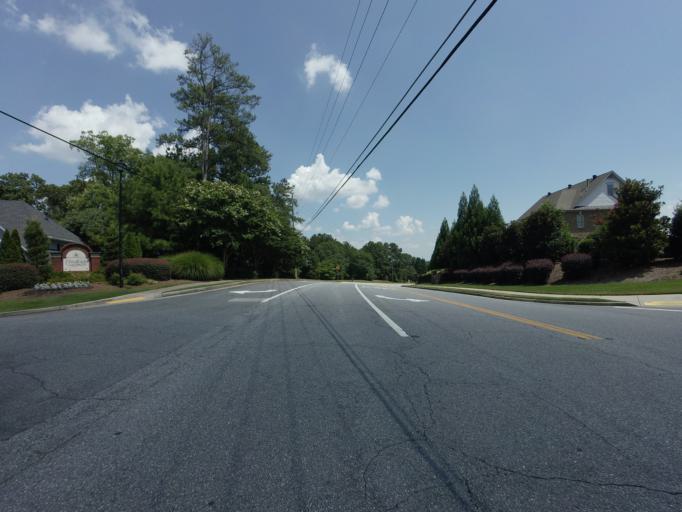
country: US
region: Georgia
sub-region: Fulton County
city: Johns Creek
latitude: 34.0404
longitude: -84.2014
